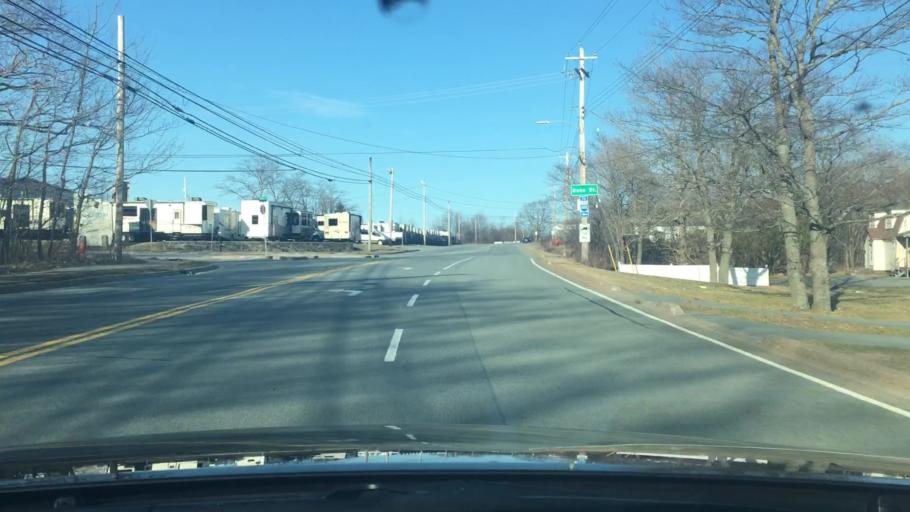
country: CA
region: Nova Scotia
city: Dartmouth
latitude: 44.7457
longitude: -63.6357
